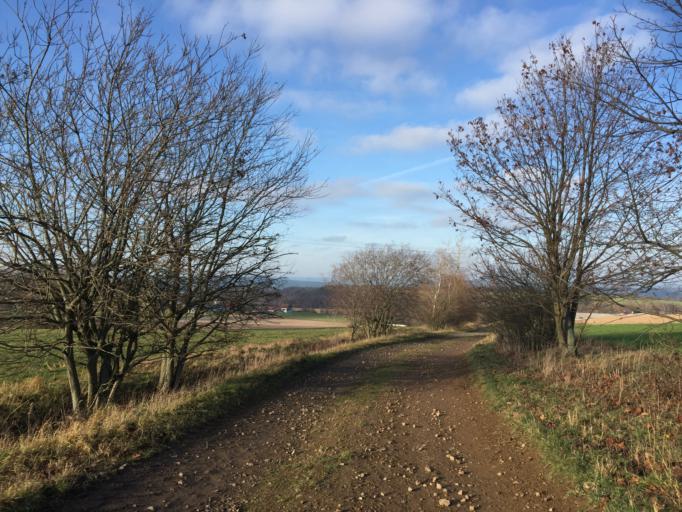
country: DE
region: Thuringia
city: Ranis
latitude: 50.6617
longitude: 11.5840
